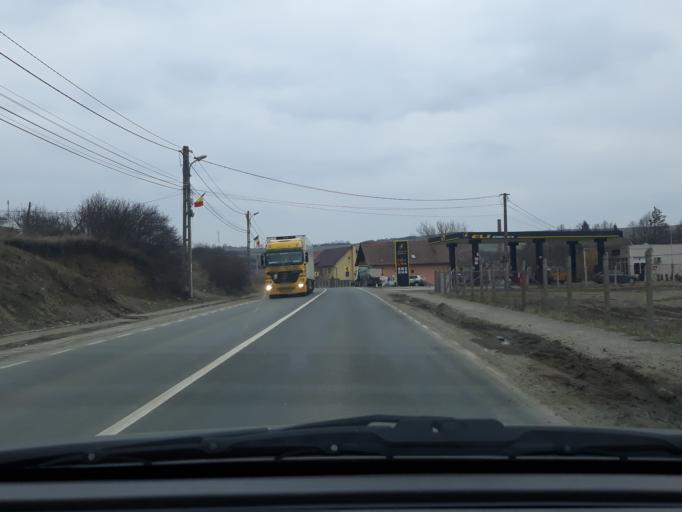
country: RO
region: Salaj
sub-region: Oras Simleu Silvaniei
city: Simleu Silvaniei
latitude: 47.2263
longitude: 22.7717
